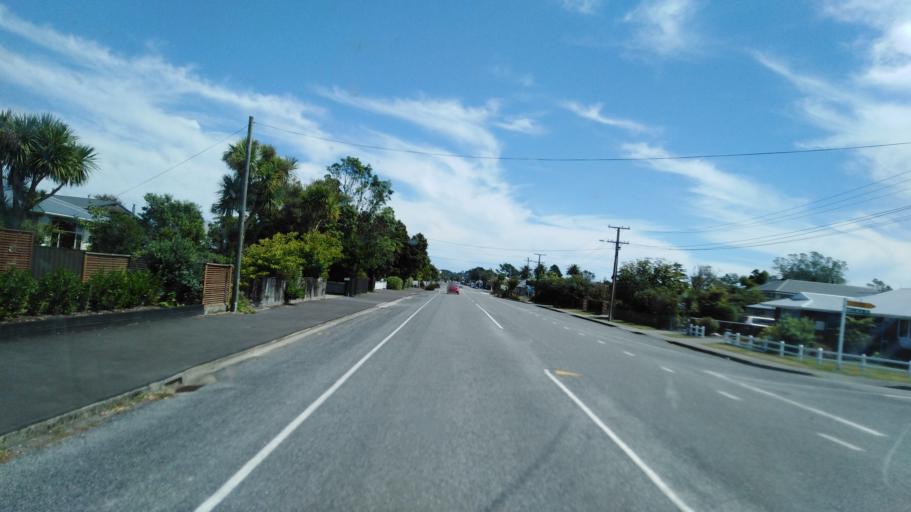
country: NZ
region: West Coast
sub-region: Buller District
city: Westport
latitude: -41.7543
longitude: 171.6076
